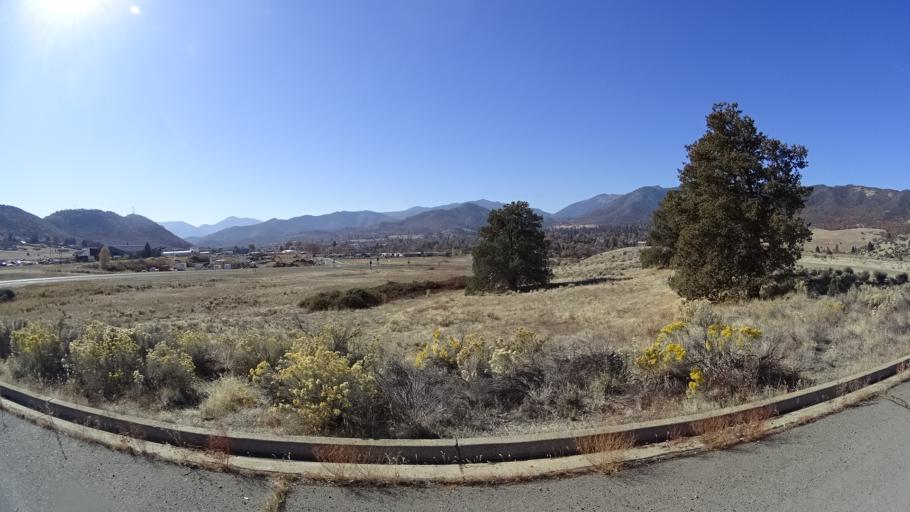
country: US
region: California
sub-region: Siskiyou County
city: Yreka
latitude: 41.7395
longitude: -122.6211
